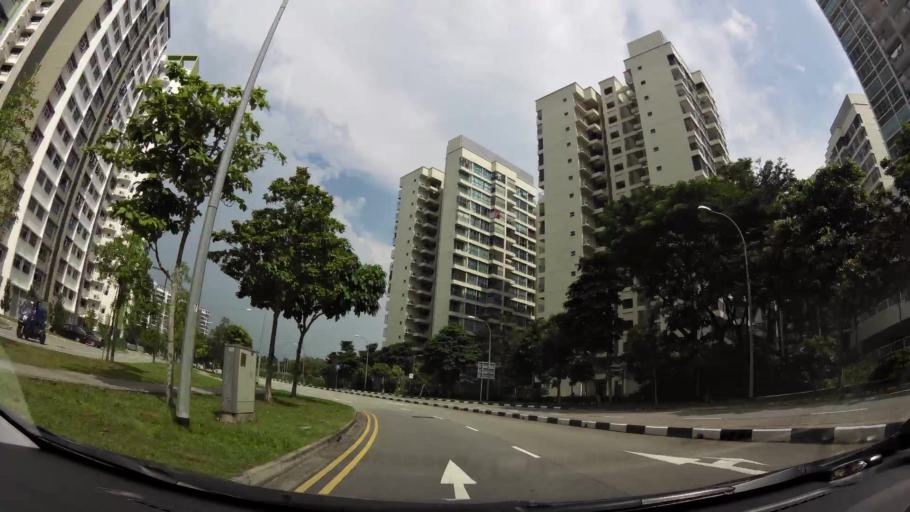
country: SG
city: Singapore
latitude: 1.3576
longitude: 103.9392
